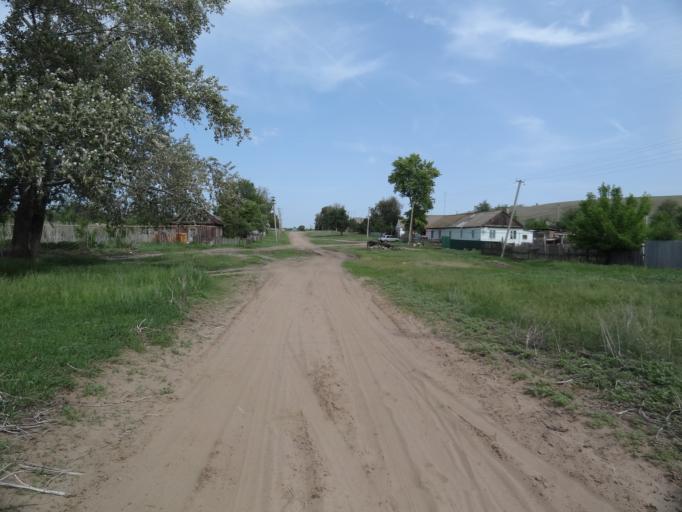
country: RU
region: Saratov
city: Krasnoarmeysk
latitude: 51.1571
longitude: 45.9285
